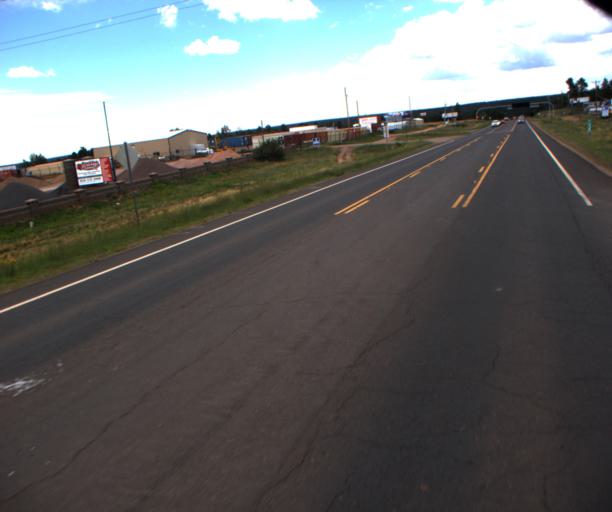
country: US
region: Arizona
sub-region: Navajo County
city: Linden
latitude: 34.2854
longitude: -110.1209
